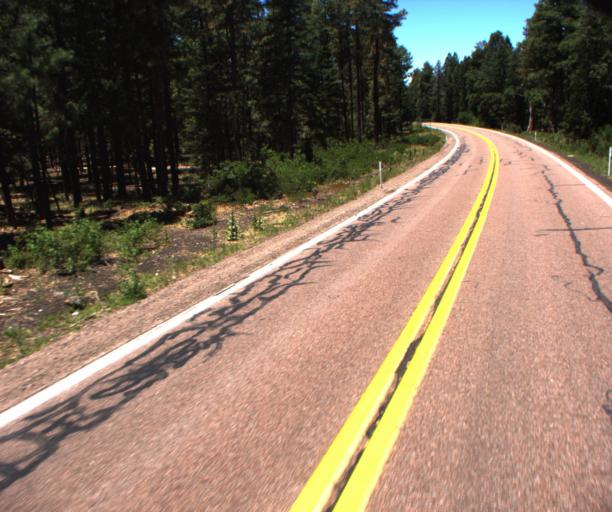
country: US
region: Arizona
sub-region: Gila County
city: Pine
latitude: 34.4563
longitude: -111.4031
